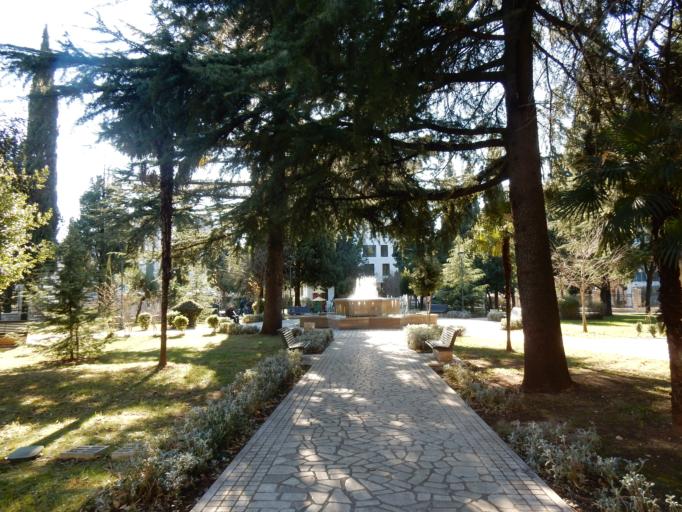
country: ME
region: Podgorica
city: Podgorica
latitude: 42.4382
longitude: 19.2629
